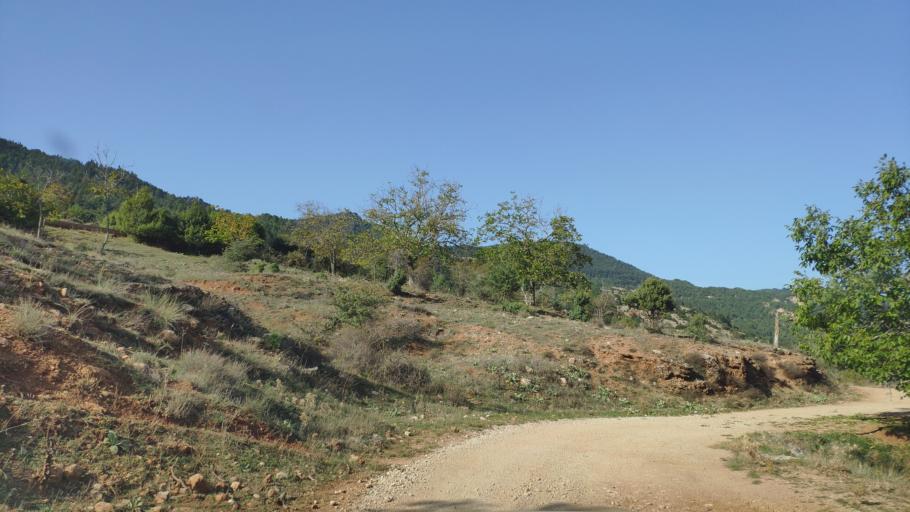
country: GR
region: West Greece
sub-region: Nomos Achaias
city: Aiyira
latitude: 37.9888
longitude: 22.3477
